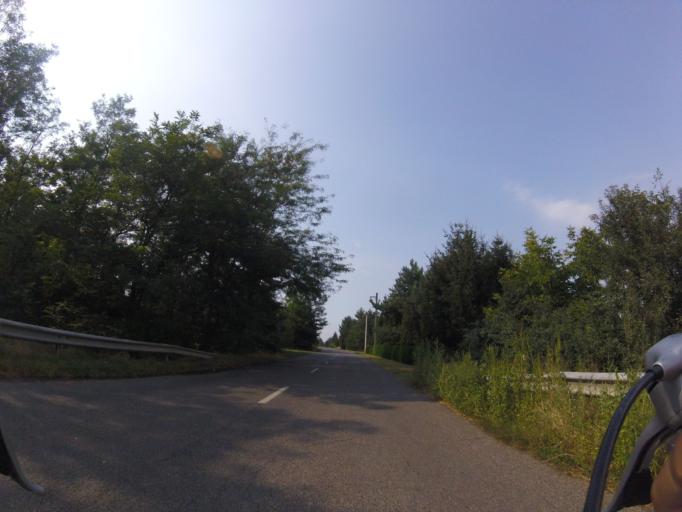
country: HU
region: Szabolcs-Szatmar-Bereg
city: Kotaj
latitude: 48.0309
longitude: 21.7551
